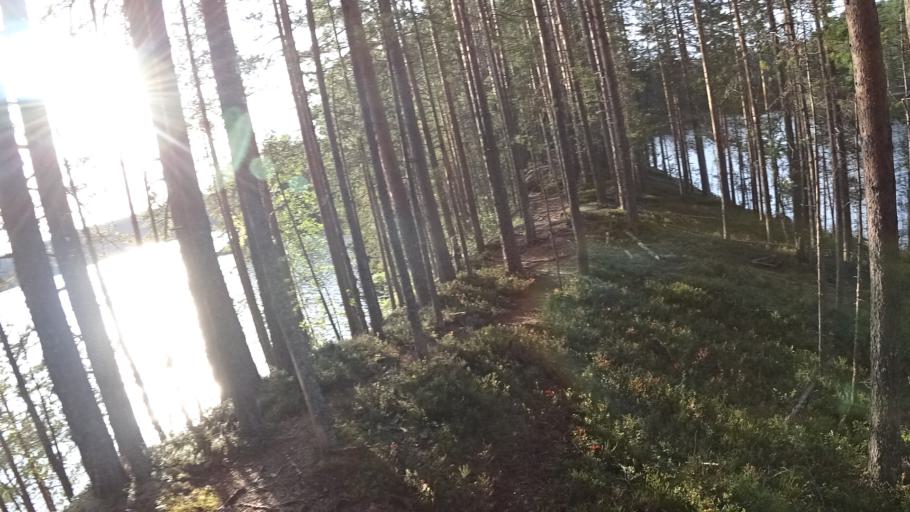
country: FI
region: North Karelia
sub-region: Joensuu
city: Ilomantsi
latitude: 62.5775
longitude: 31.1714
